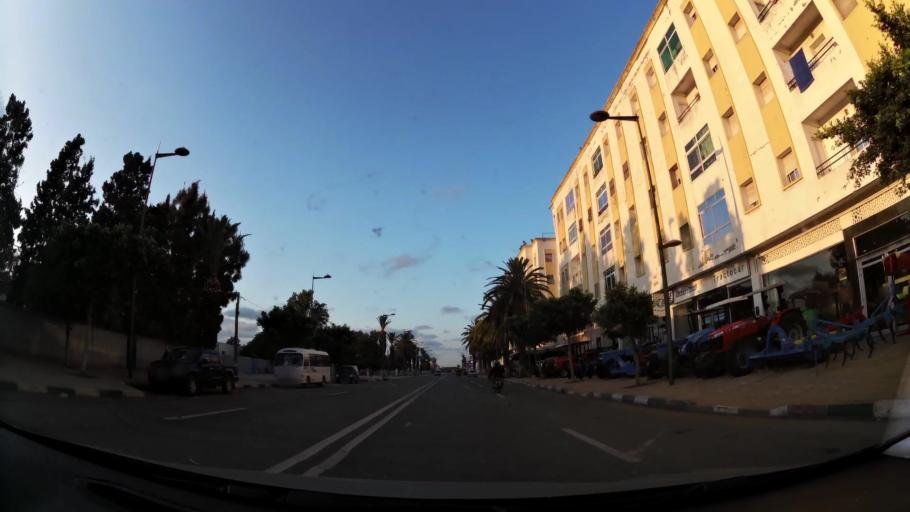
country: MA
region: Gharb-Chrarda-Beni Hssen
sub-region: Kenitra Province
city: Kenitra
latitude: 34.2733
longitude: -6.5575
